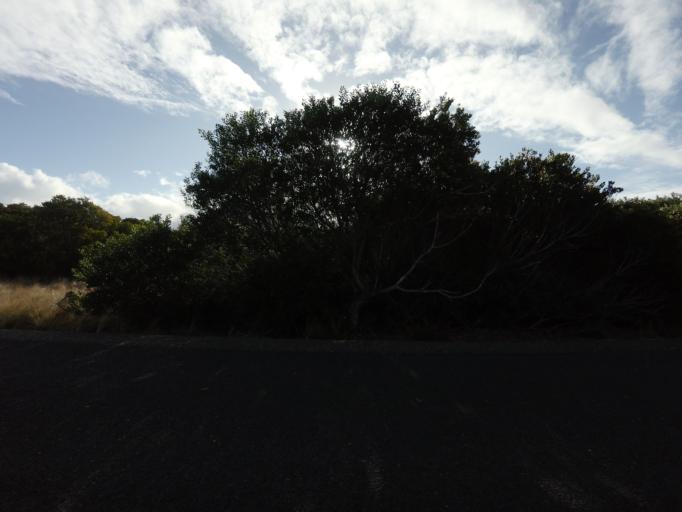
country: AU
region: Tasmania
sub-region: Break O'Day
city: St Helens
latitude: -42.0958
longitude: 148.2310
